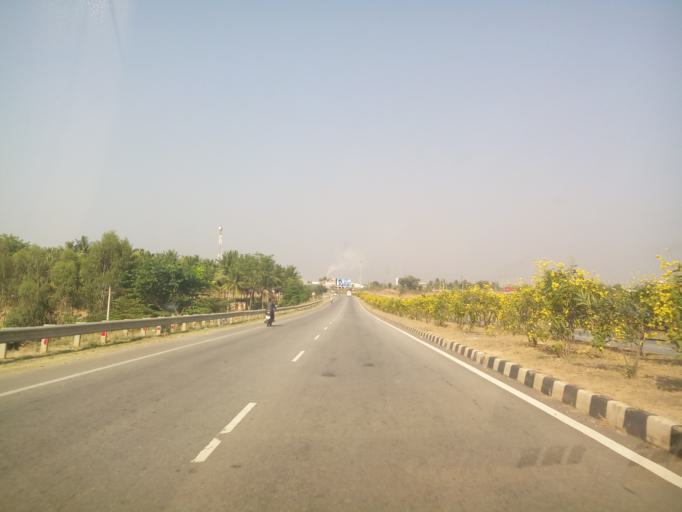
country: IN
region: Karnataka
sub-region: Tumkur
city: Kunigal
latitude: 13.0352
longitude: 77.0909
